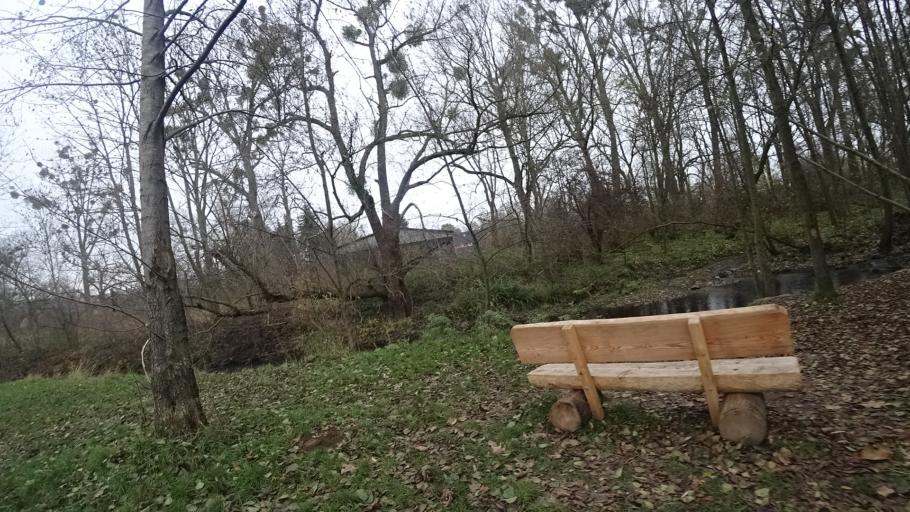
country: DE
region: Lower Saxony
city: Lauenau
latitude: 52.2709
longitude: 9.3655
